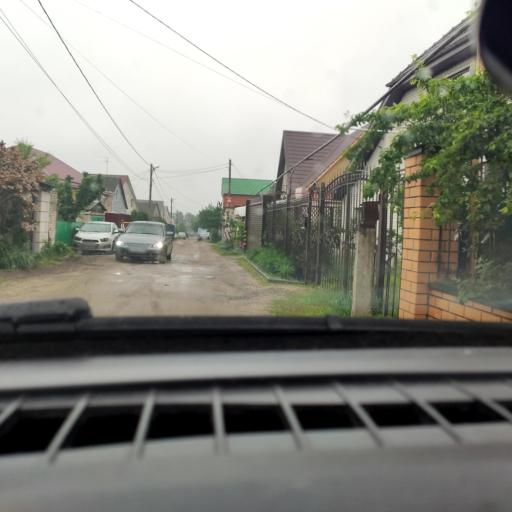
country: RU
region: Voronezj
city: Podgornoye
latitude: 51.7408
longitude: 39.1582
